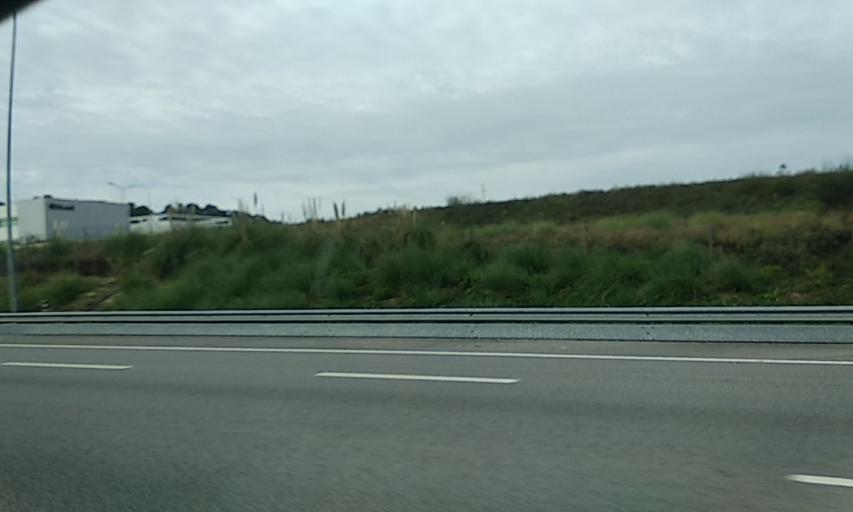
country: PT
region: Porto
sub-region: Trofa
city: Sao Romao do Coronado
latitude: 41.2605
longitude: -8.5657
